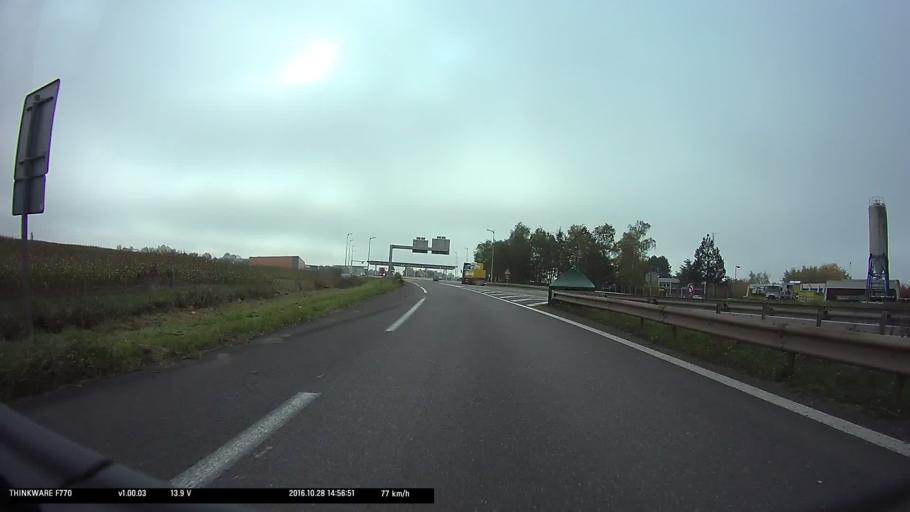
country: FR
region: Lorraine
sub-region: Departement de la Moselle
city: Phalsbourg
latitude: 48.7742
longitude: 7.2420
